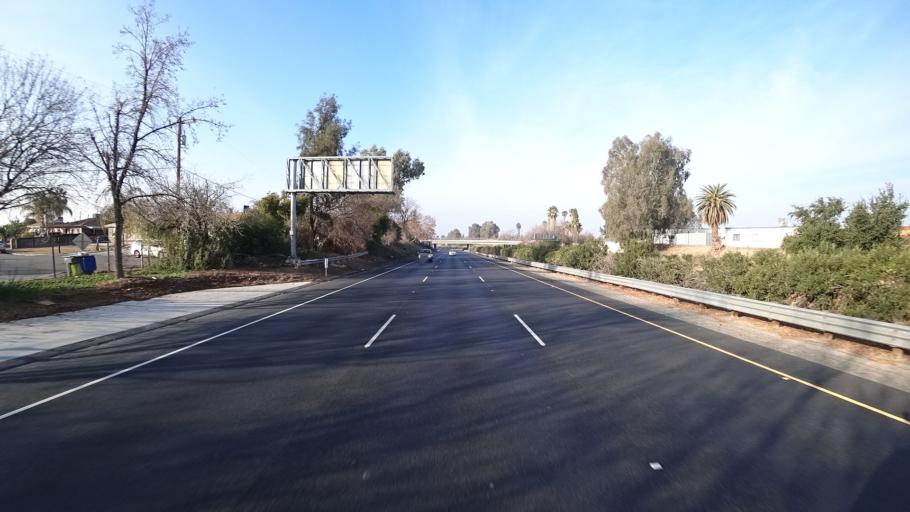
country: US
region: California
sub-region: Kern County
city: Bakersfield
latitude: 35.3928
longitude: -118.9736
